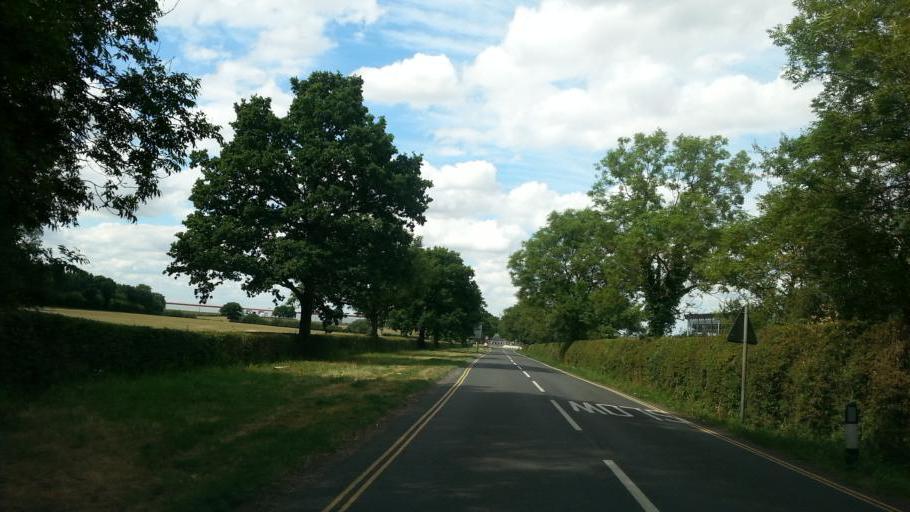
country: GB
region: England
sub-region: Northamptonshire
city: Silverstone
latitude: 52.0655
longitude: -1.0258
